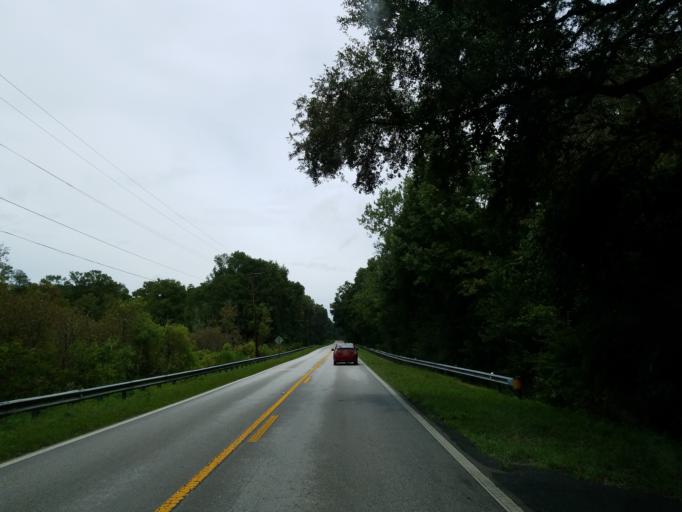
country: US
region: Florida
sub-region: Sumter County
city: Bushnell
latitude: 28.6926
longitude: -82.2113
